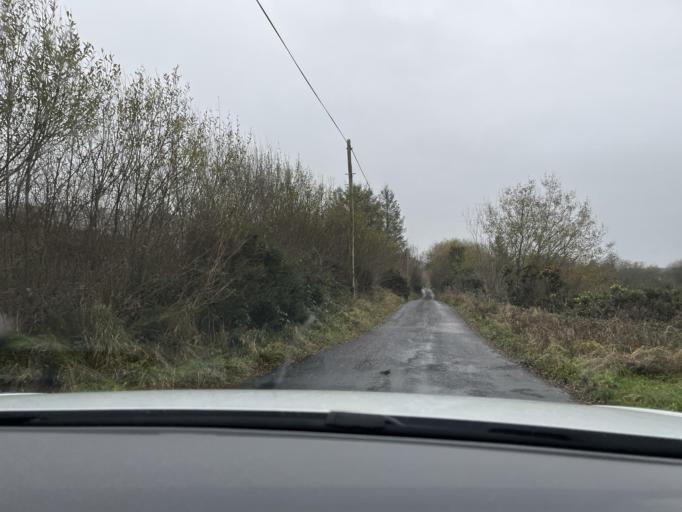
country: IE
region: Connaught
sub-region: County Leitrim
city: Manorhamilton
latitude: 54.2853
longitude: -8.0862
